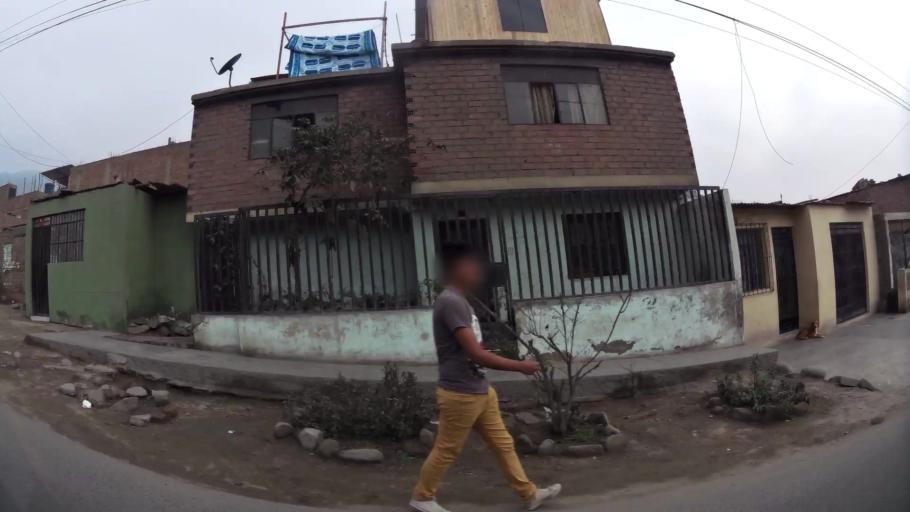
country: PE
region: Lima
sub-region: Lima
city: Independencia
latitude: -11.9815
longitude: -76.9792
